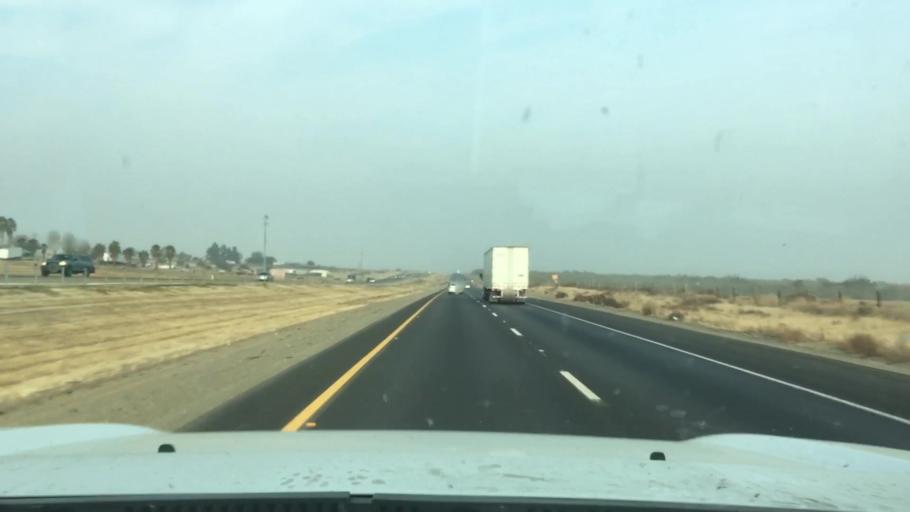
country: US
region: California
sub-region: Stanislaus County
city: Patterson
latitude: 37.5625
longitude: -121.2964
